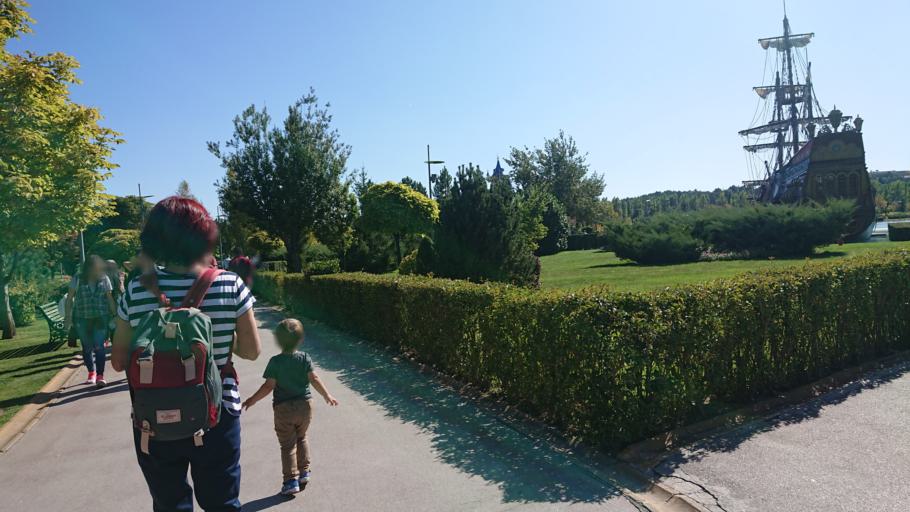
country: TR
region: Eskisehir
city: Eskisehir
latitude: 39.7634
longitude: 30.4738
